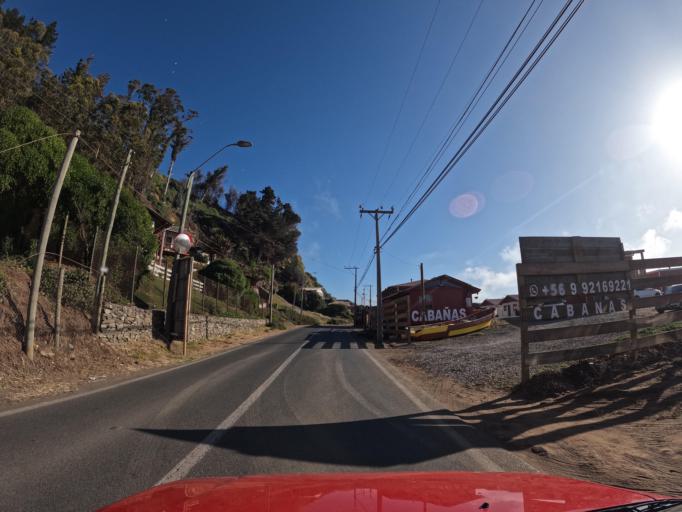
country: CL
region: Maule
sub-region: Provincia de Talca
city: Constitucion
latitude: -34.9068
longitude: -72.1808
